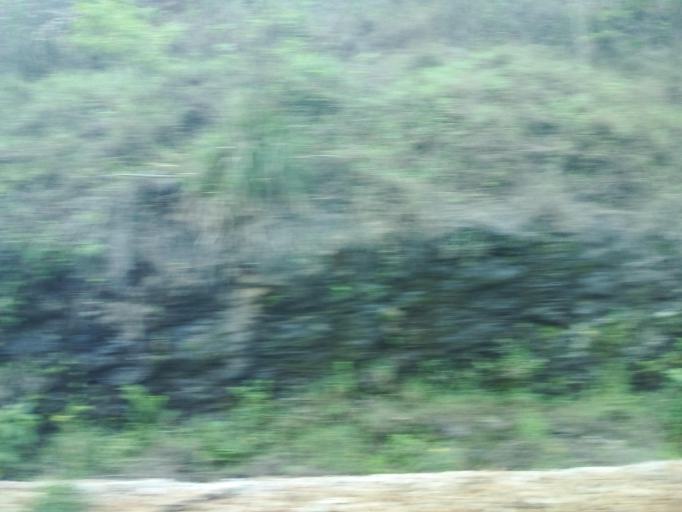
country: BR
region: Minas Gerais
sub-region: Joao Monlevade
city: Joao Monlevade
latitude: -19.8654
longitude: -43.1179
